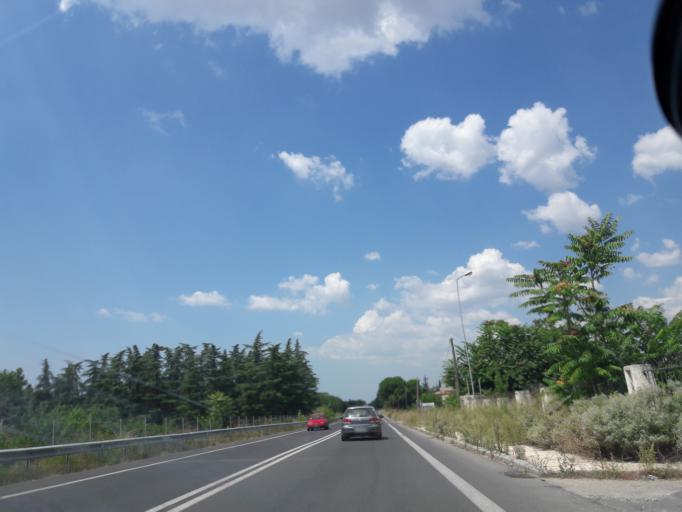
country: GR
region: Central Macedonia
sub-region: Nomos Thessalonikis
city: Souroti
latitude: 40.5080
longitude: 23.0867
